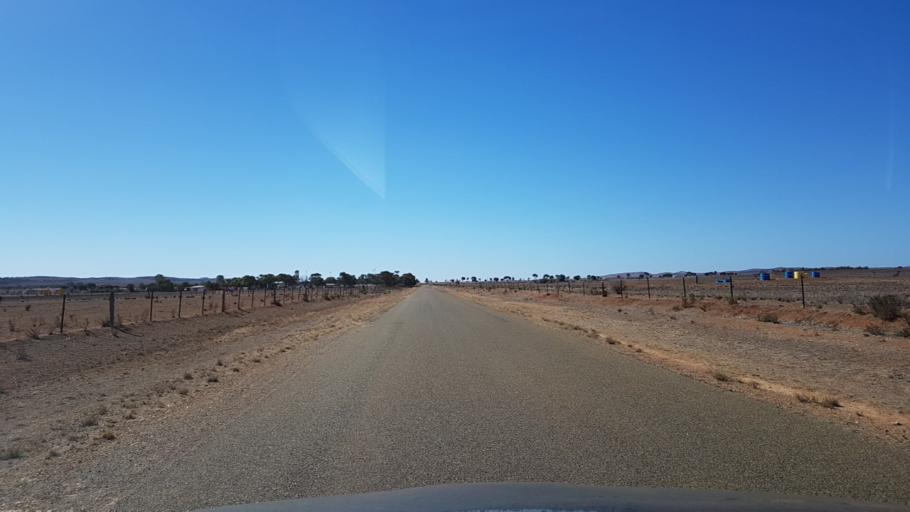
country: AU
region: South Australia
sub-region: Peterborough
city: Peterborough
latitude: -32.9793
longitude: 138.8523
